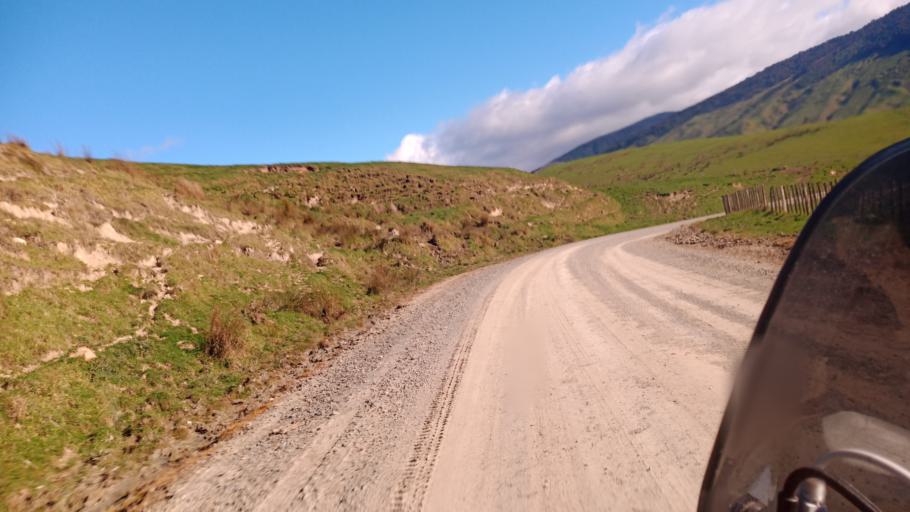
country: NZ
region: Hawke's Bay
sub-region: Wairoa District
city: Wairoa
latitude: -38.7730
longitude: 177.2644
